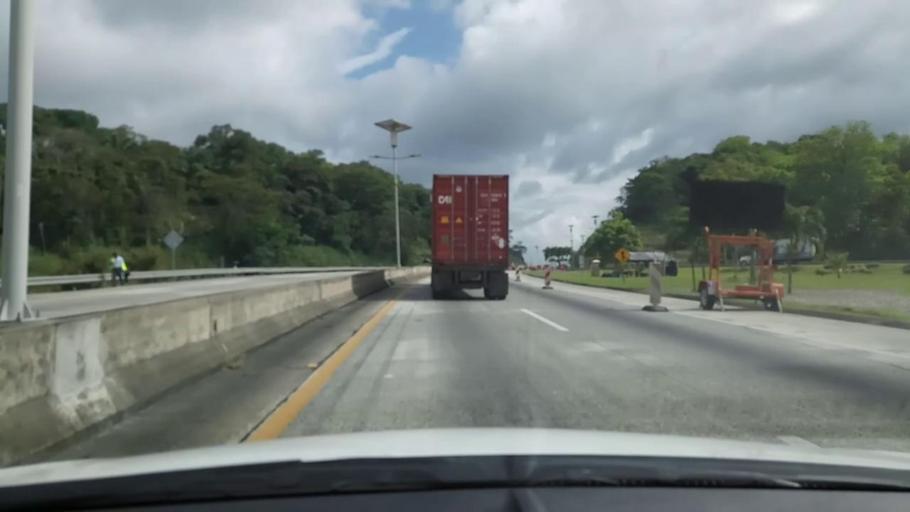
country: PA
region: Panama
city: Chilibre
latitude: 9.1237
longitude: -79.6185
